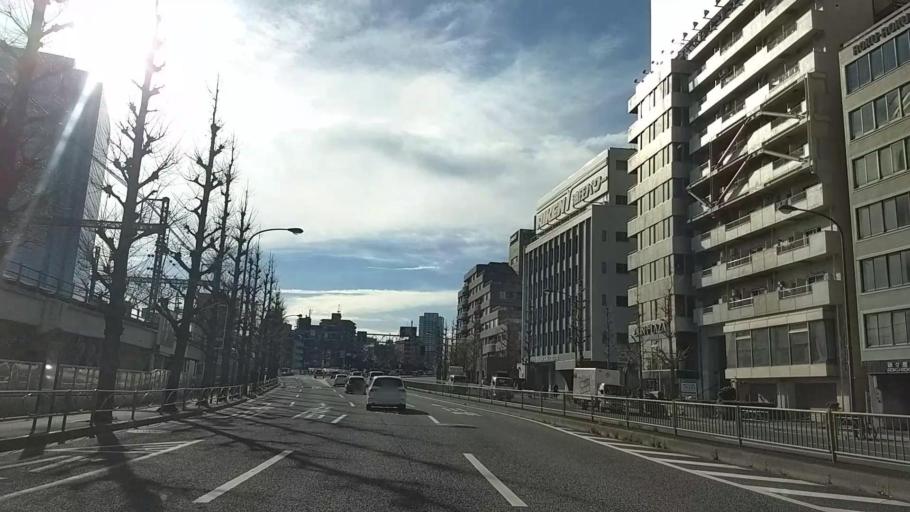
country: JP
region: Tokyo
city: Tokyo
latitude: 35.6265
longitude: 139.7378
